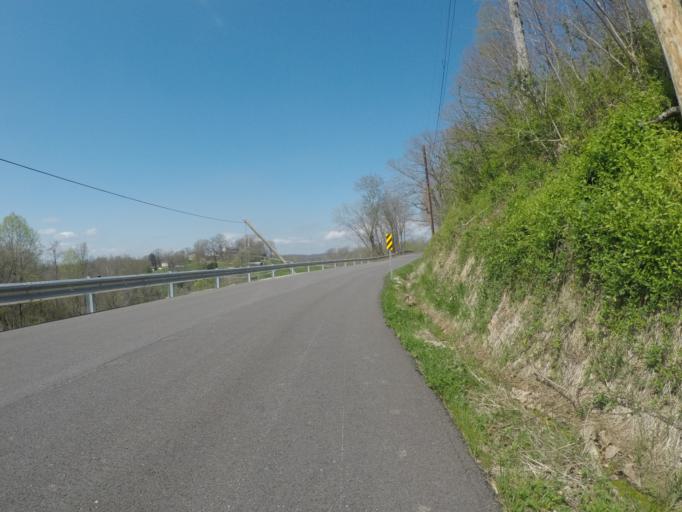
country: US
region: Ohio
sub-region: Lawrence County
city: Burlington
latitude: 38.3832
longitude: -82.5330
